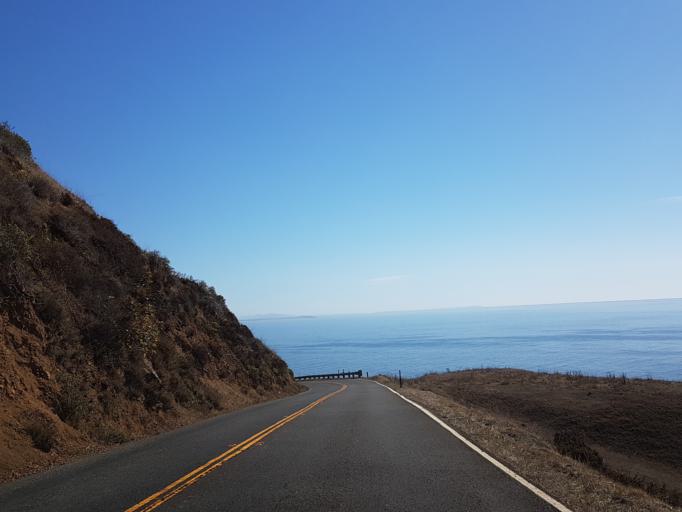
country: US
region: California
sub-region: Sonoma County
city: Monte Rio
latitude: 38.4932
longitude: -123.1968
